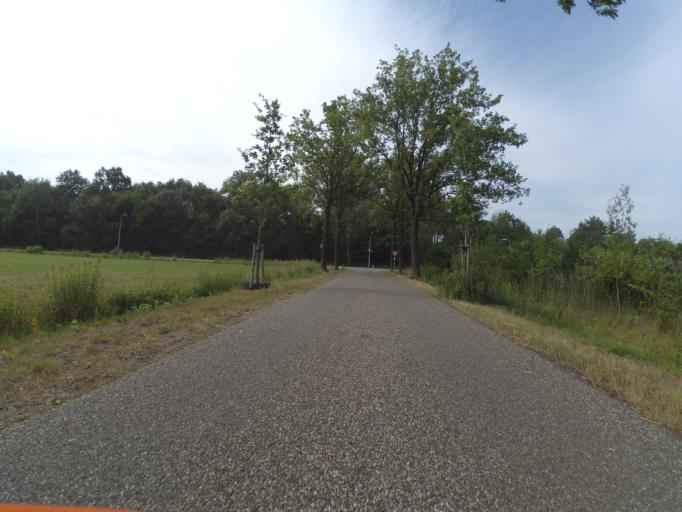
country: NL
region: Overijssel
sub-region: Gemeente Haaksbergen
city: Haaksbergen
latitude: 52.2073
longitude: 6.7270
